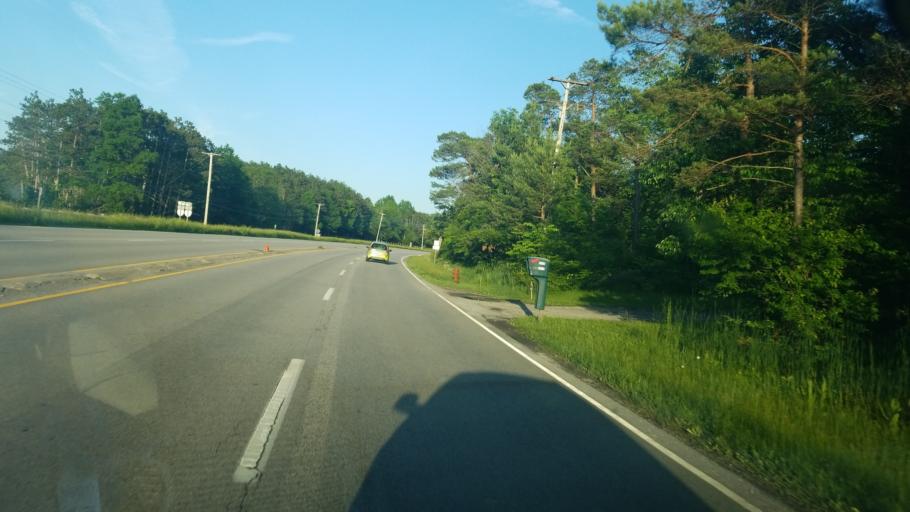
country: US
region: Ohio
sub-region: Mahoning County
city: Austintown
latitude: 41.1001
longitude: -80.8216
